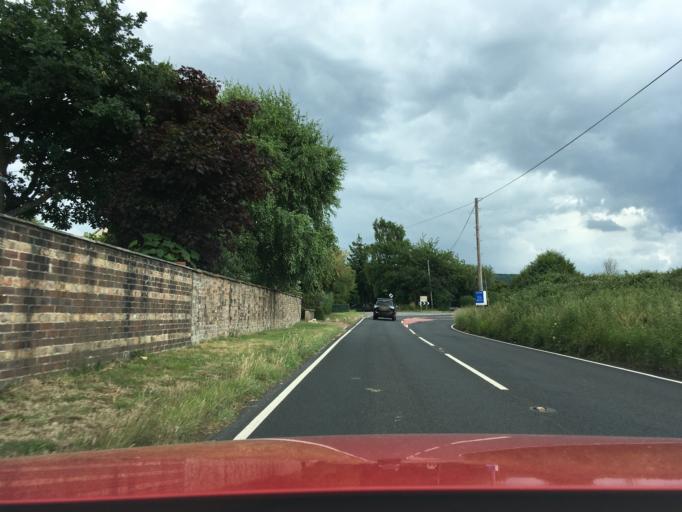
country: GB
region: England
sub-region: Gloucestershire
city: Stonehouse
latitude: 51.7811
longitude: -2.2883
